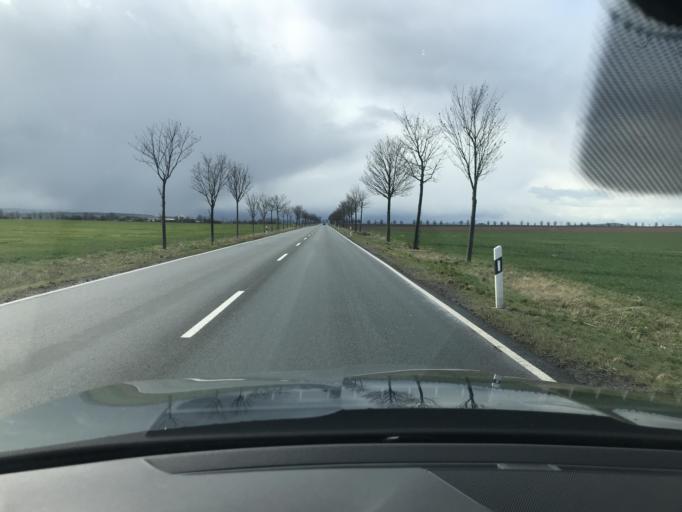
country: DE
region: Saxony-Anhalt
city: Hoym
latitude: 51.7845
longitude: 11.2827
